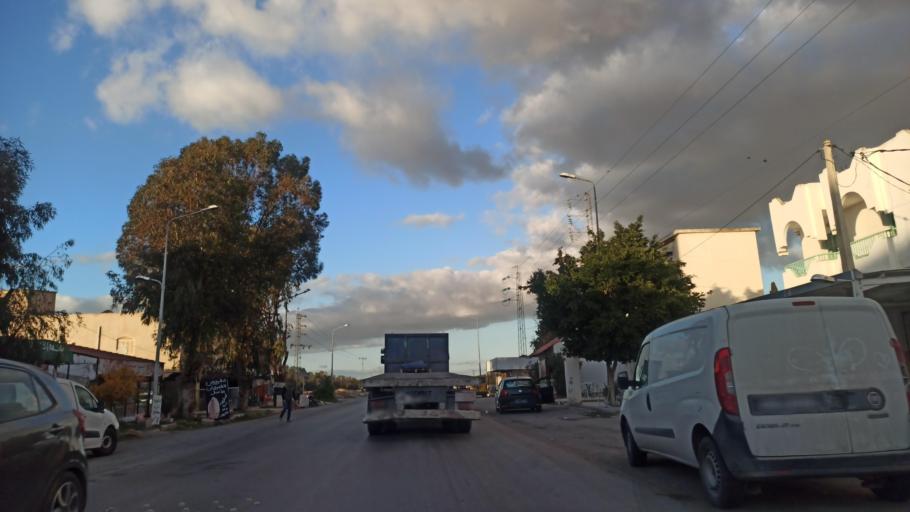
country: TN
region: Susah
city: Sidi Bou Ali
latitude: 35.9350
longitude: 10.3009
